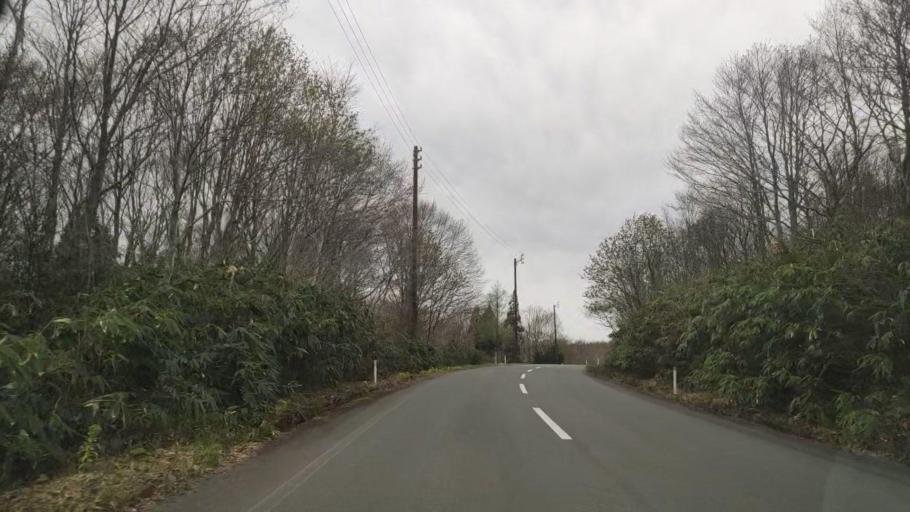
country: JP
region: Akita
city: Hanawa
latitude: 40.4070
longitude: 140.8542
